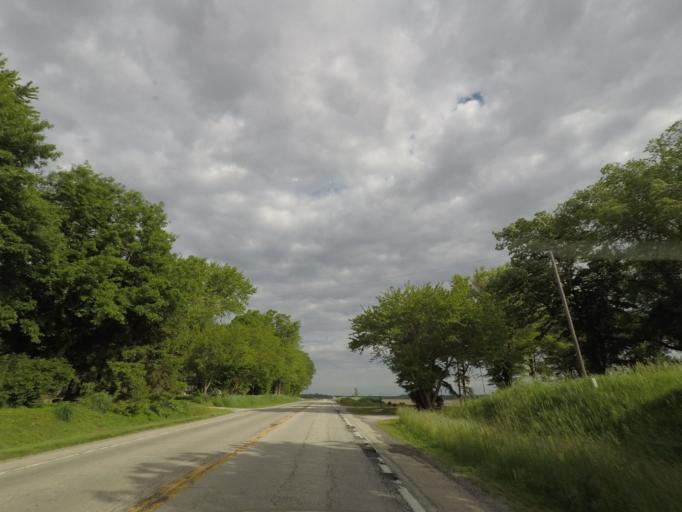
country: US
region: Illinois
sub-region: Logan County
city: Lincoln
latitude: 40.0954
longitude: -89.3141
